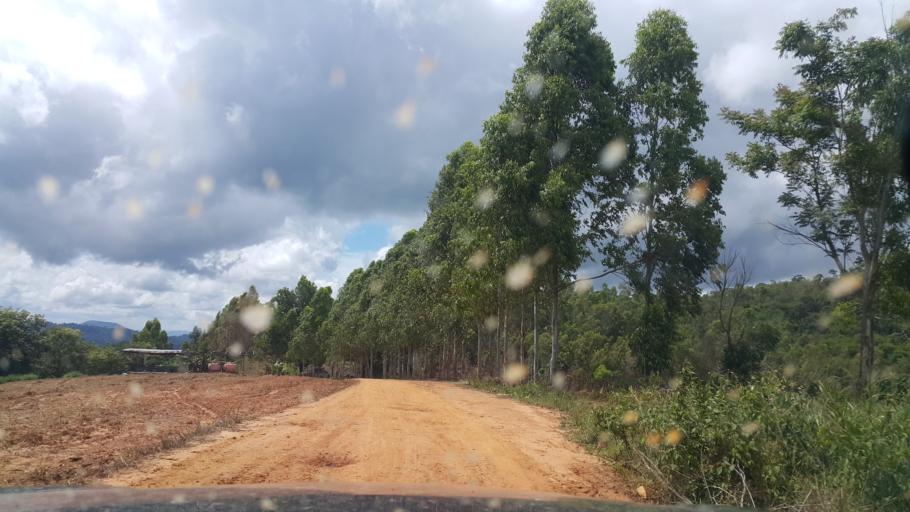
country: TH
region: Loei
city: Na Haeo
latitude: 17.5981
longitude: 100.9005
